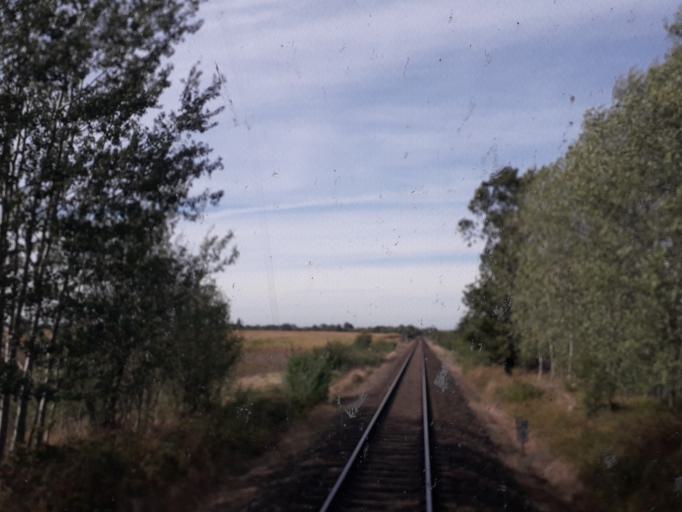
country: DE
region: Brandenburg
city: Velten
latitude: 52.7134
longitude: 13.1295
